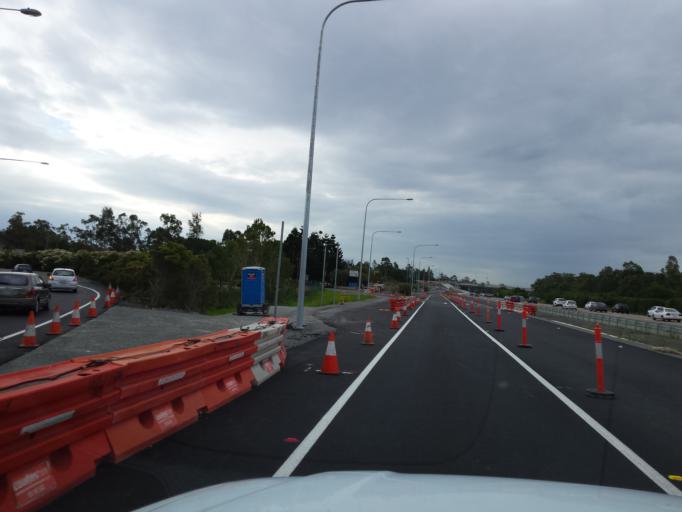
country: AU
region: Queensland
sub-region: Gold Coast
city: Oxenford
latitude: -27.8629
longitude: 153.3108
